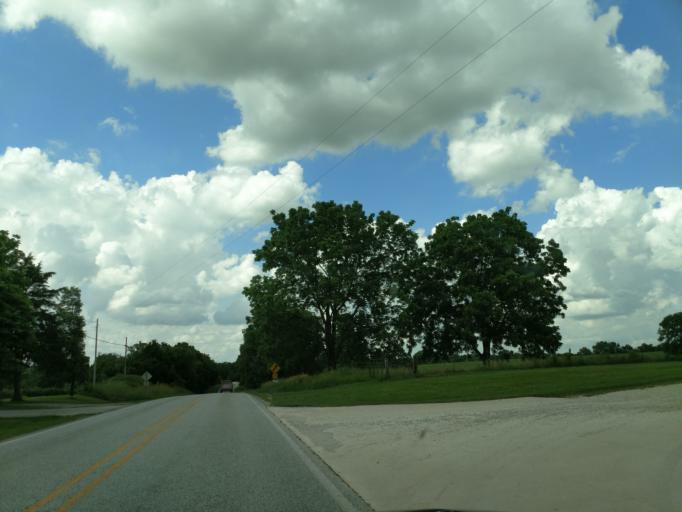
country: US
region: Arkansas
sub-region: Carroll County
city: Berryville
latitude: 36.4030
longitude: -93.5660
